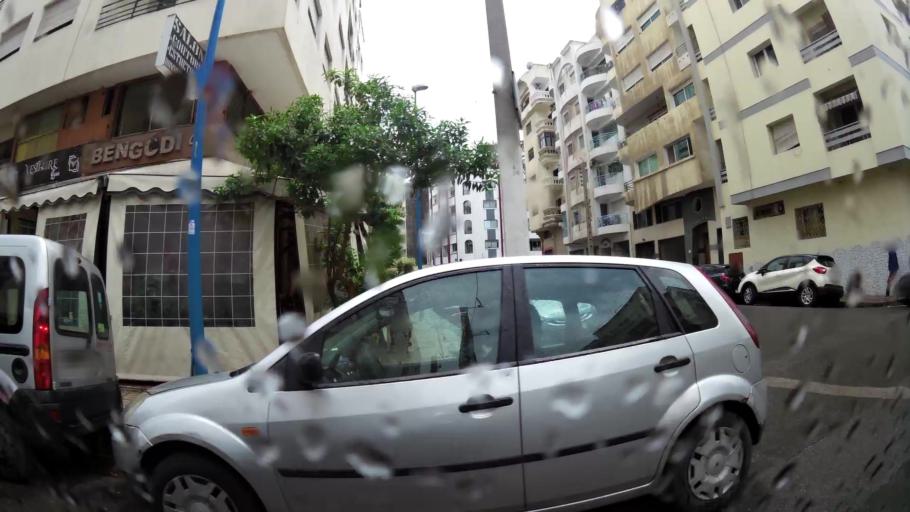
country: MA
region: Grand Casablanca
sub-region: Casablanca
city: Casablanca
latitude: 33.5759
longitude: -7.6145
